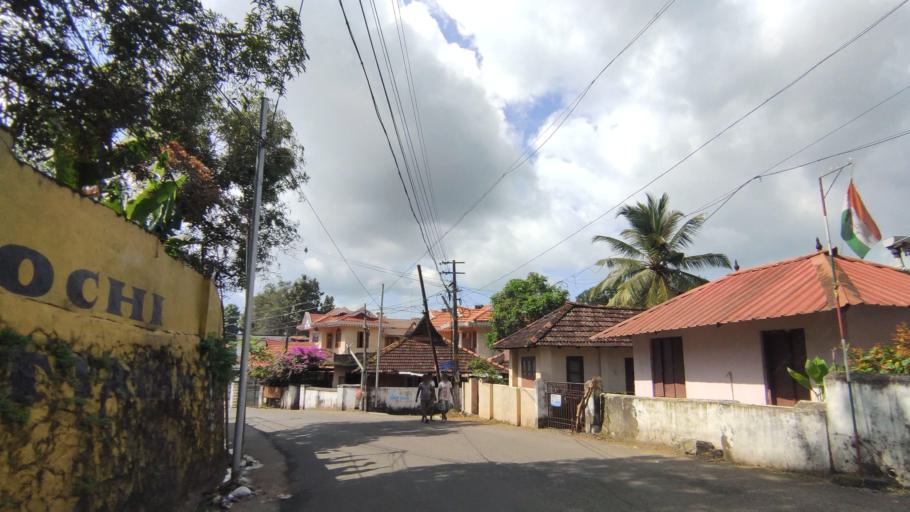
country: IN
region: Kerala
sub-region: Kottayam
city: Kottayam
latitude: 9.5870
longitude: 76.5288
